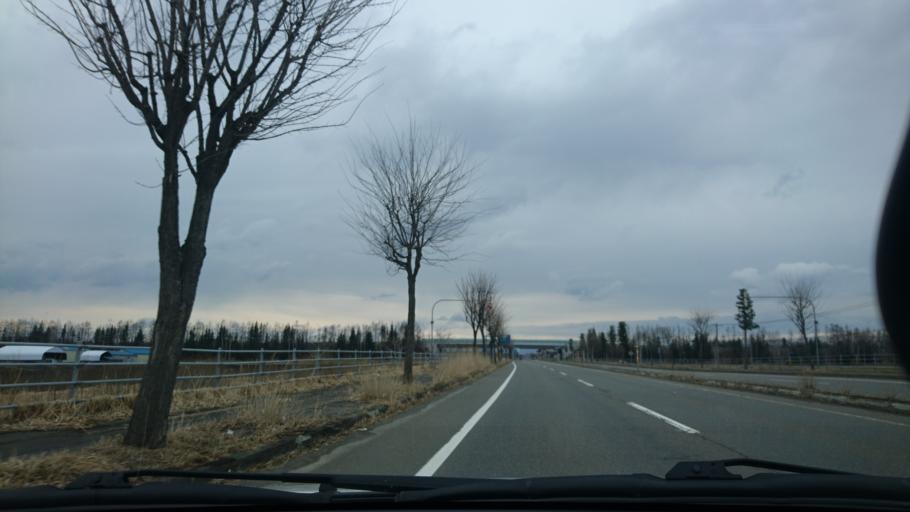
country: JP
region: Hokkaido
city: Otofuke
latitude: 42.9783
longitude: 143.1843
